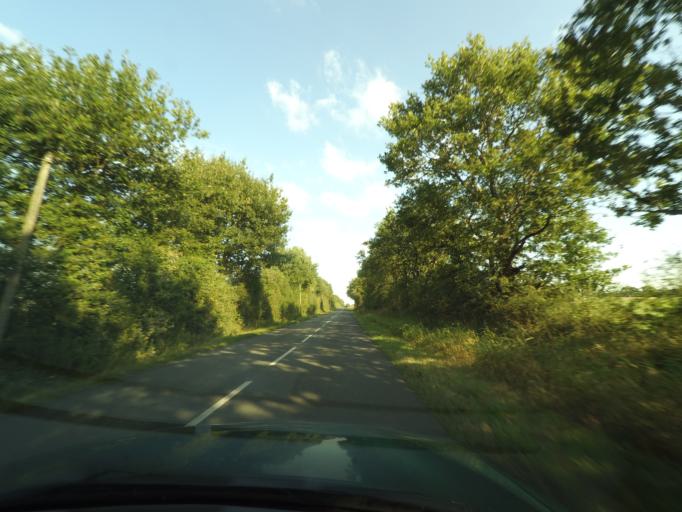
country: FR
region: Pays de la Loire
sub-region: Departement de la Loire-Atlantique
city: La Limouziniere
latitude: 47.0217
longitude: -1.6063
